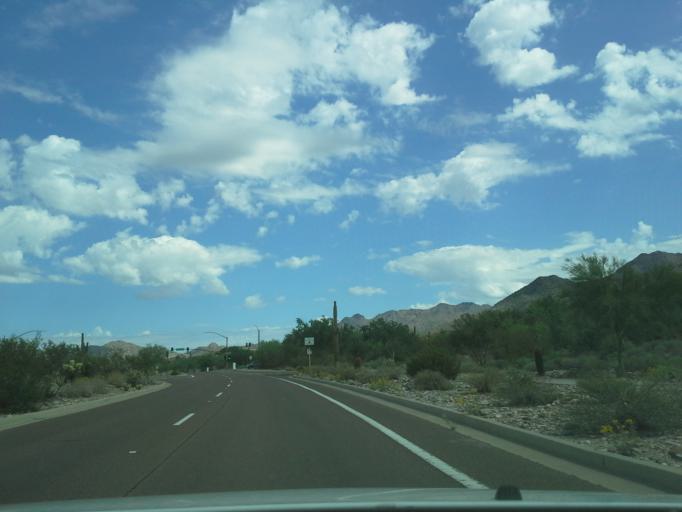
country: US
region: Arizona
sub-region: Maricopa County
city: Scottsdale
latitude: 33.6324
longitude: -111.8605
